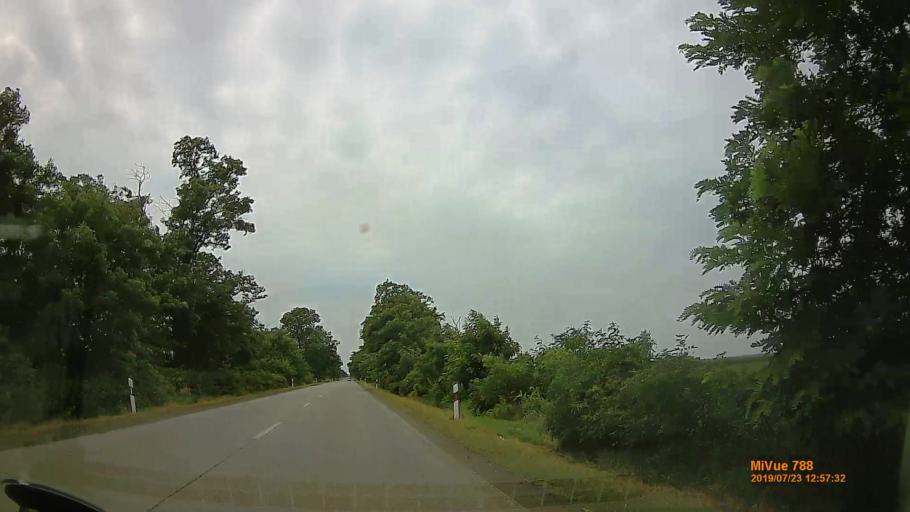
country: HU
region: Szabolcs-Szatmar-Bereg
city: Nagycserkesz
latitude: 47.9581
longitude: 21.4758
